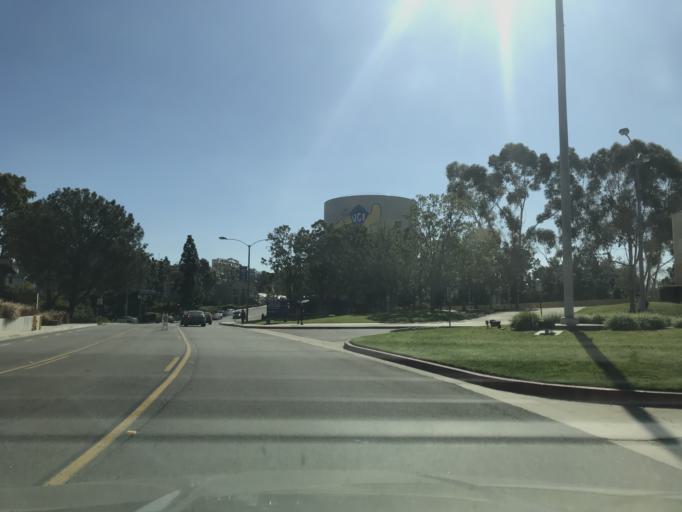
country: US
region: California
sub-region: Orange County
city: Irvine
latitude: 33.6499
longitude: -117.8461
